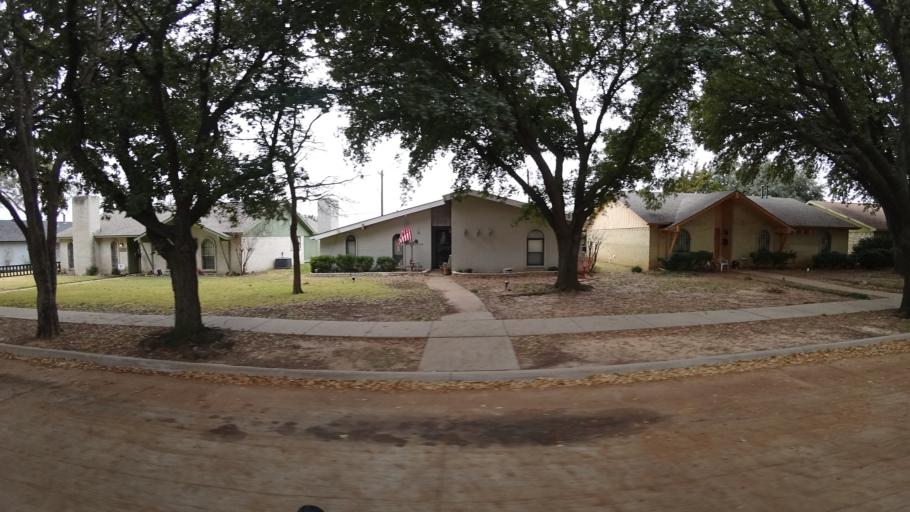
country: US
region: Texas
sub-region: Denton County
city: Lewisville
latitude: 33.0381
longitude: -97.0291
